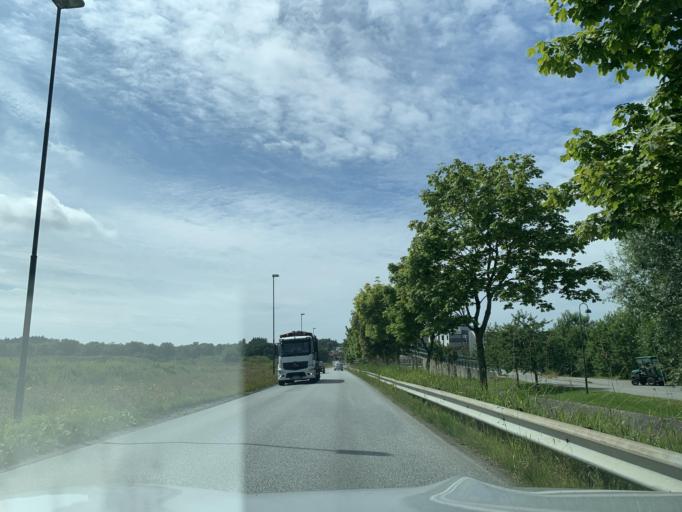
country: NO
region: Rogaland
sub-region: Sola
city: Sola
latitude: 58.8942
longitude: 5.6853
